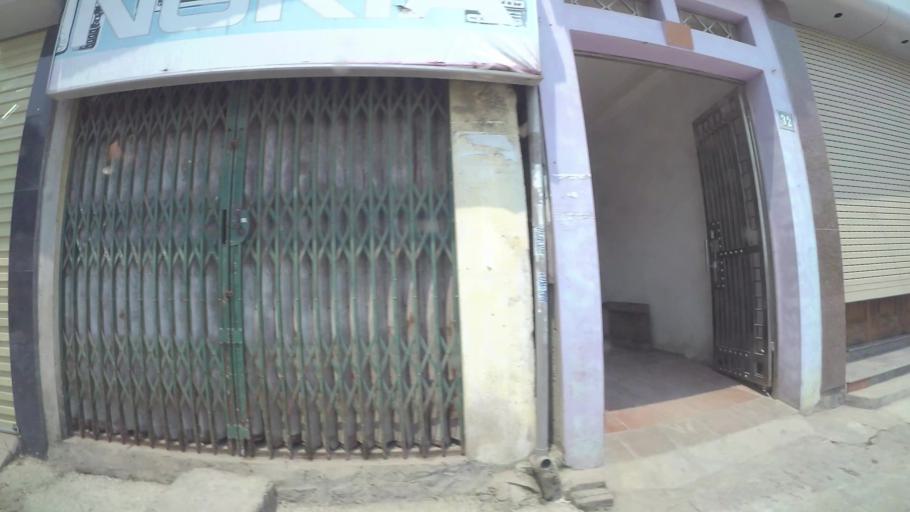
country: VN
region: Ha Noi
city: Van Dien
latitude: 20.9511
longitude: 105.8300
